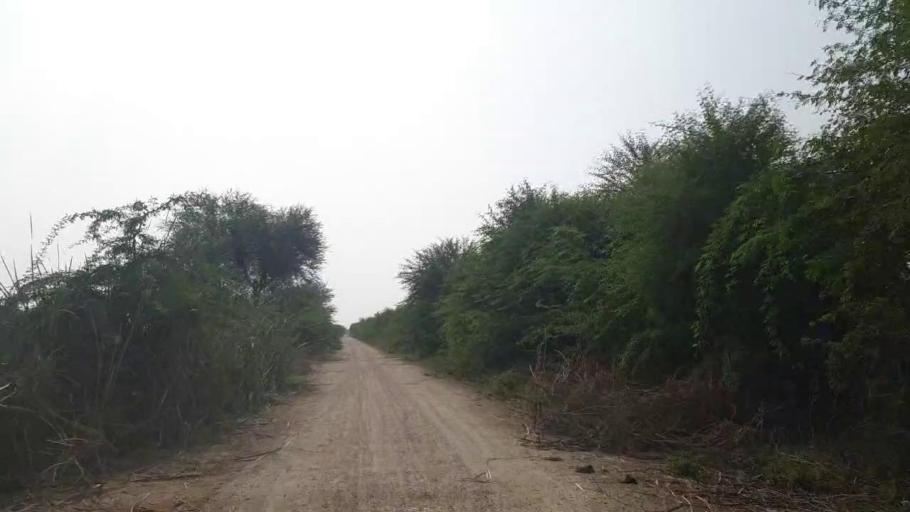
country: PK
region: Sindh
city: Badin
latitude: 24.6108
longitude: 68.7213
